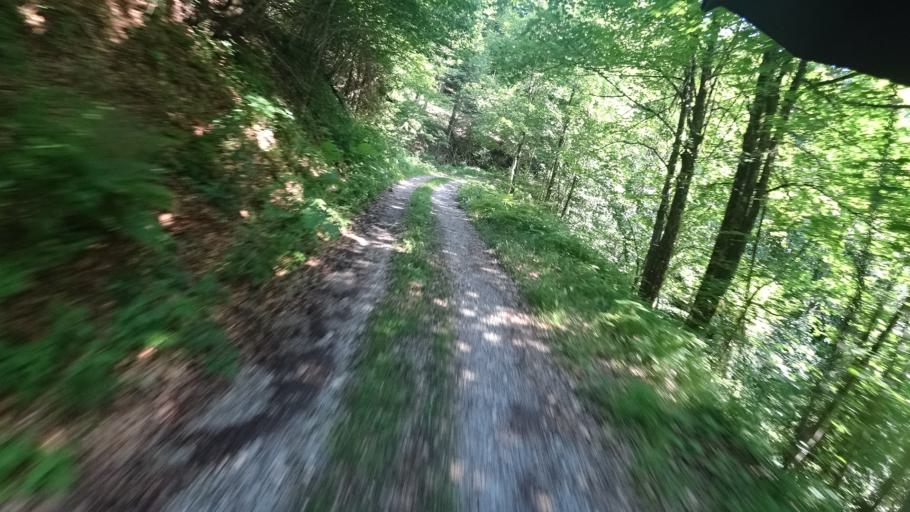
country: SI
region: Osilnica
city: Osilnica
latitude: 45.4685
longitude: 14.6983
